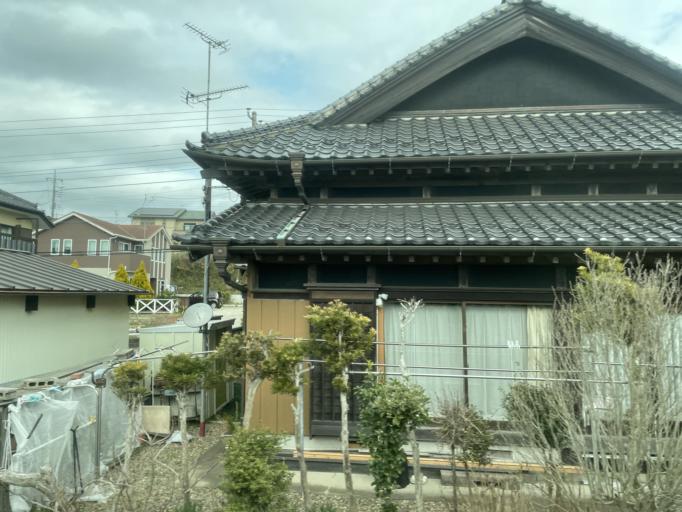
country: JP
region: Chiba
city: Narita
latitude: 35.8291
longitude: 140.2565
